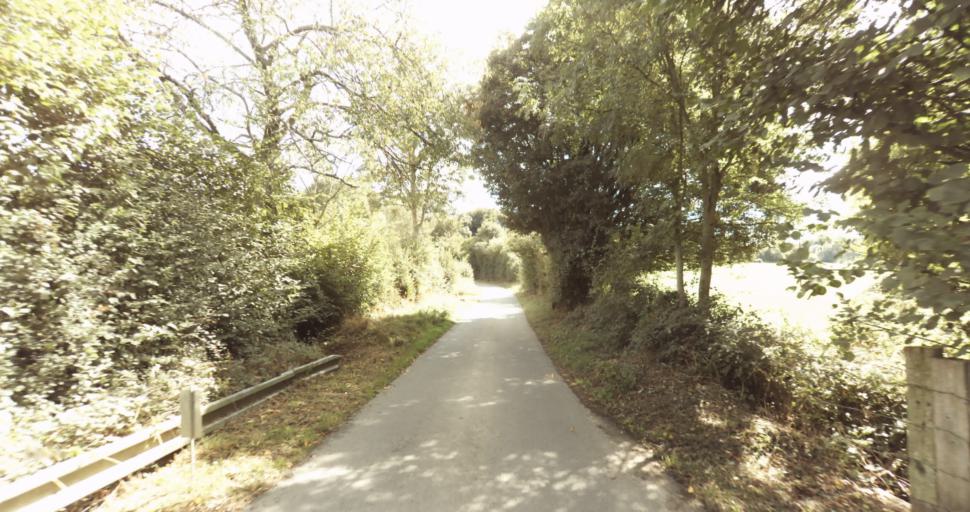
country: FR
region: Lower Normandy
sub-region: Departement de l'Orne
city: Gace
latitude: 48.9077
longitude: 0.3491
